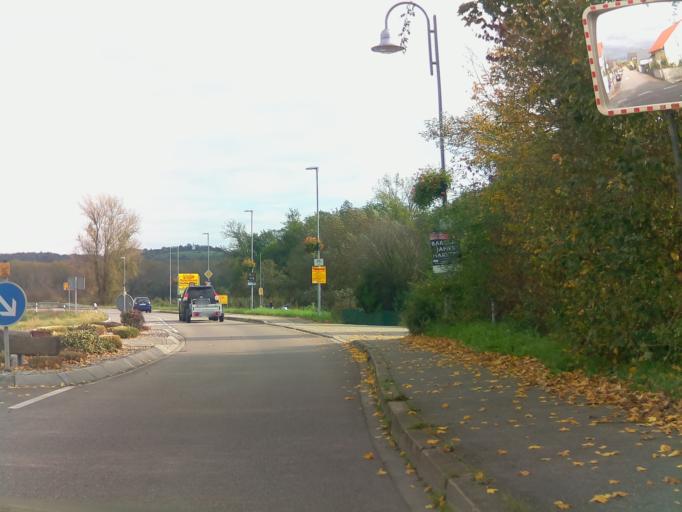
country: DE
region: Baden-Wuerttemberg
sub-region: Karlsruhe Region
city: Weingarten
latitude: 49.0931
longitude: 8.5179
